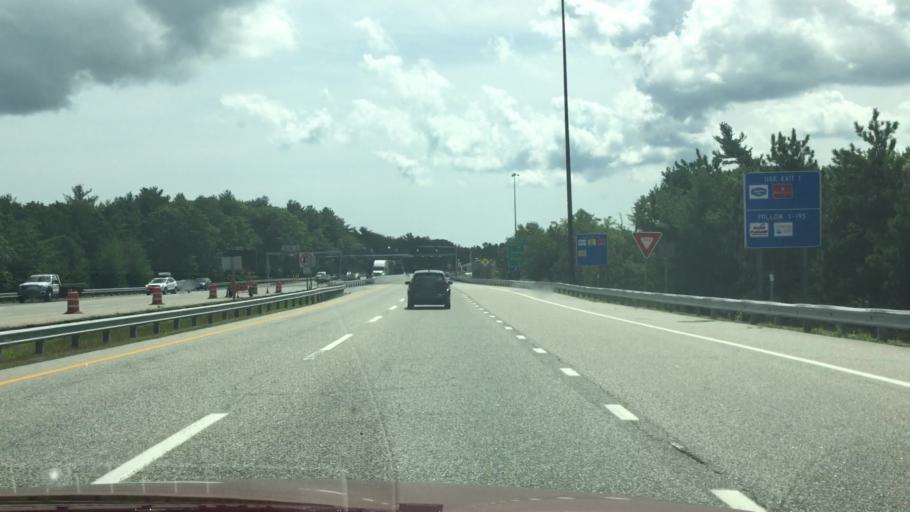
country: US
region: Maine
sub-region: York County
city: Saco
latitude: 43.5253
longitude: -70.4489
